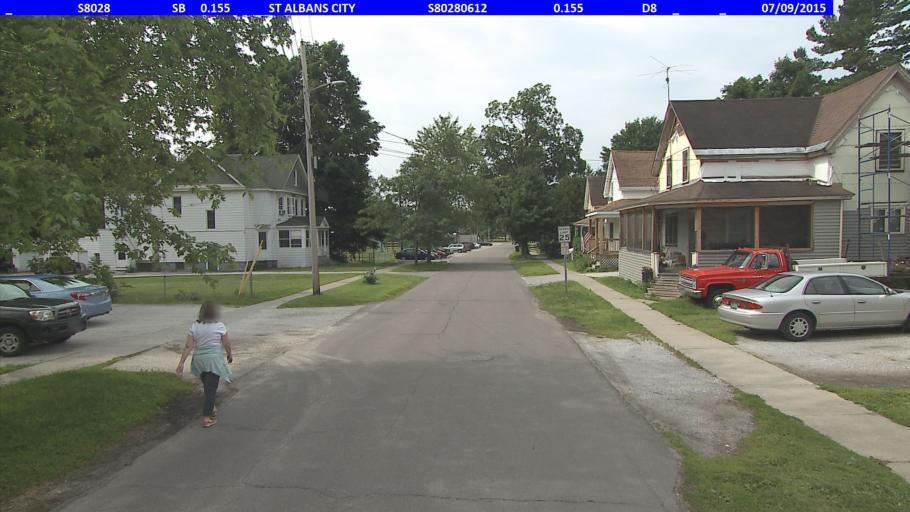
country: US
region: Vermont
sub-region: Franklin County
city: Saint Albans
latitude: 44.8110
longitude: -73.0927
